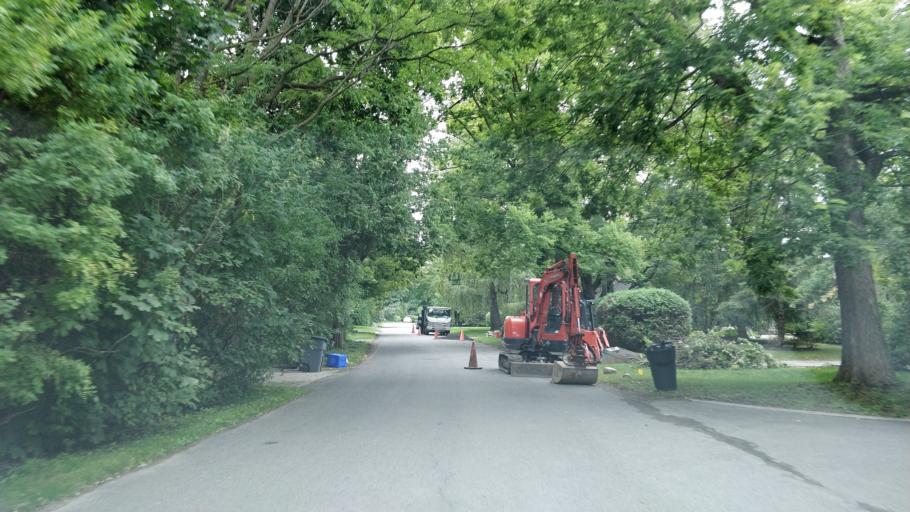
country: CA
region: Quebec
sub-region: Outaouais
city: Gatineau
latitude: 45.4510
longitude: -75.6764
